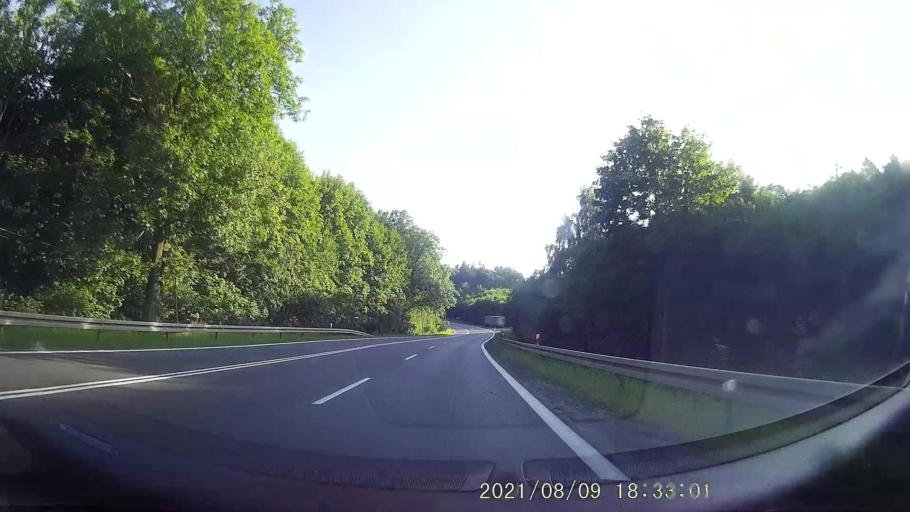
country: PL
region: Lower Silesian Voivodeship
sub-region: Powiat zabkowicki
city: Bardo
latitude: 50.4933
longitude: 16.7243
